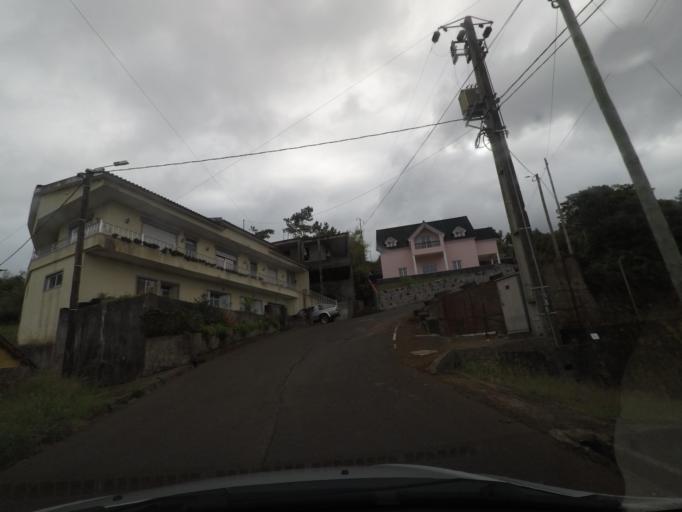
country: PT
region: Madeira
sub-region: Santana
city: Santana
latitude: 32.7872
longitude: -16.8753
